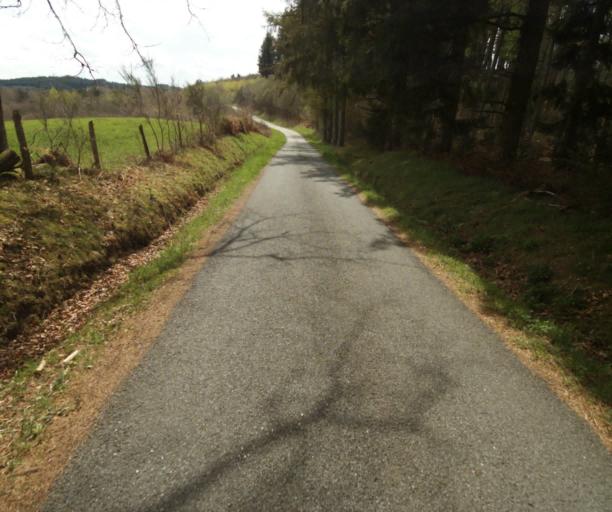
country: FR
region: Limousin
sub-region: Departement de la Correze
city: Correze
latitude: 45.3755
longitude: 1.9637
